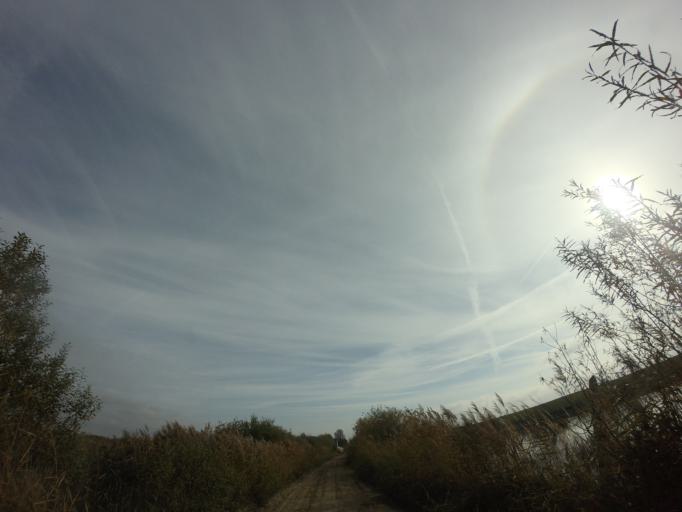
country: PL
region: West Pomeranian Voivodeship
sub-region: Powiat choszczenski
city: Drawno
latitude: 53.2350
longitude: 15.7335
